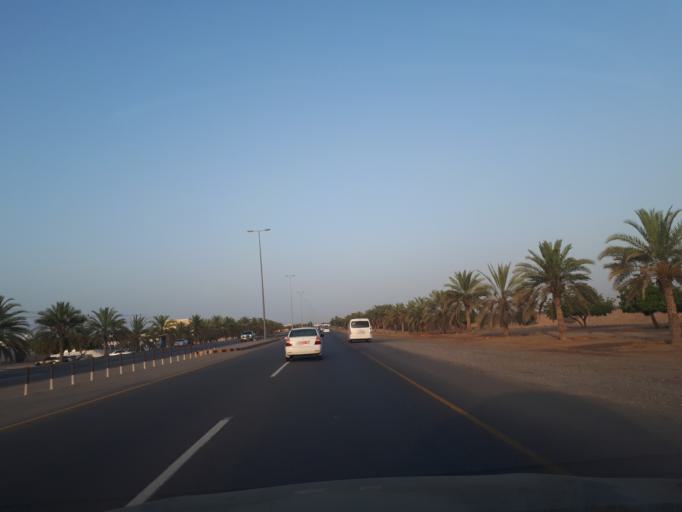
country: OM
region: Muhafazat Masqat
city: As Sib al Jadidah
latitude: 23.5895
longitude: 58.2313
